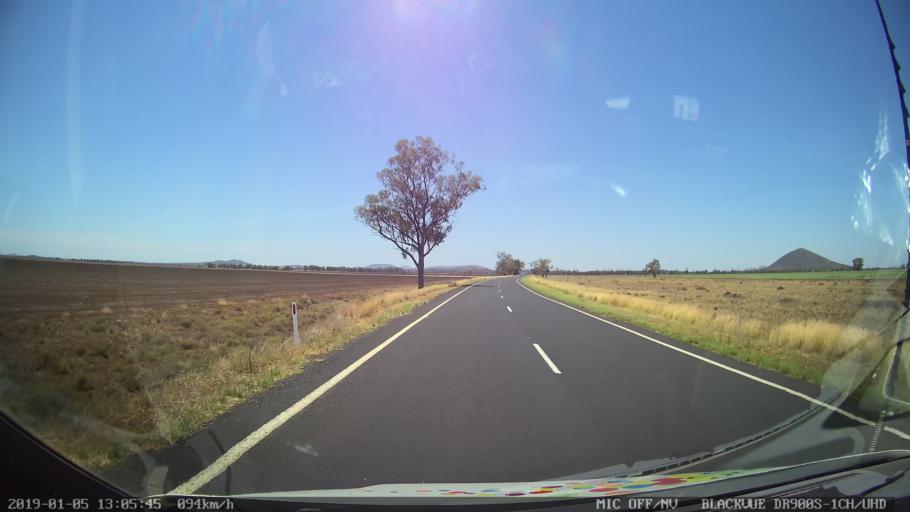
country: AU
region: New South Wales
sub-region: Gunnedah
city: Gunnedah
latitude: -31.0949
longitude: 149.8581
